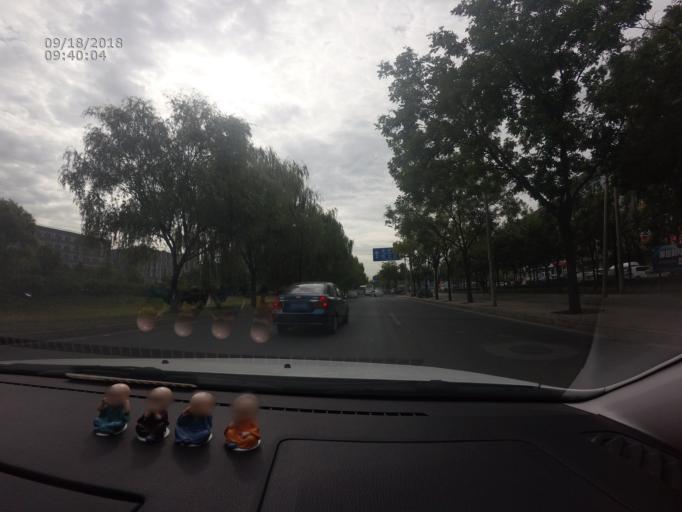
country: CN
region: Beijing
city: Xibeiwang
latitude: 40.0681
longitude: 116.2395
